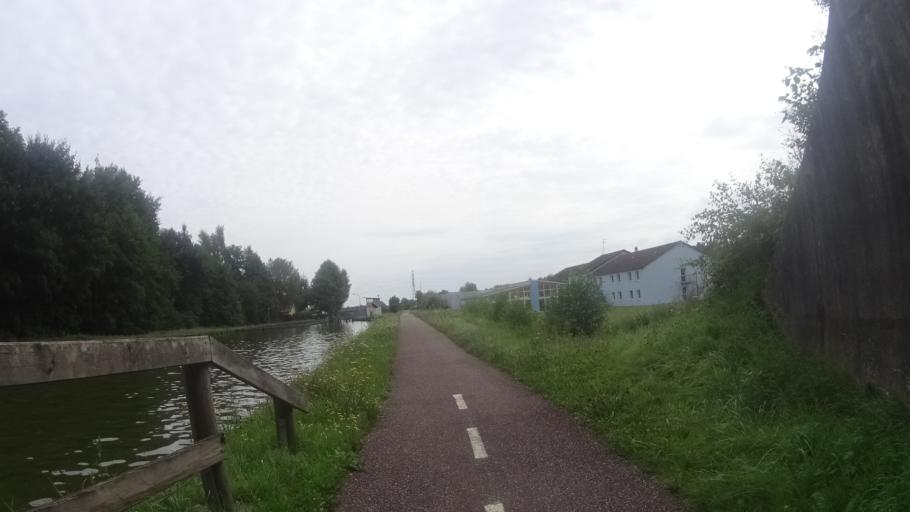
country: FR
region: Alsace
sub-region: Departement du Bas-Rhin
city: Monswiller
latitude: 48.7566
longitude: 7.3962
